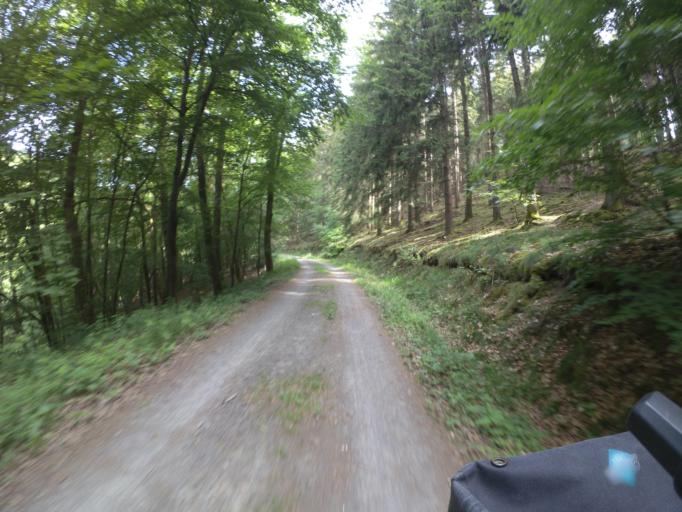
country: DE
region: Rheinland-Pfalz
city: Hermeskeil
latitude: 49.6360
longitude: 6.9269
